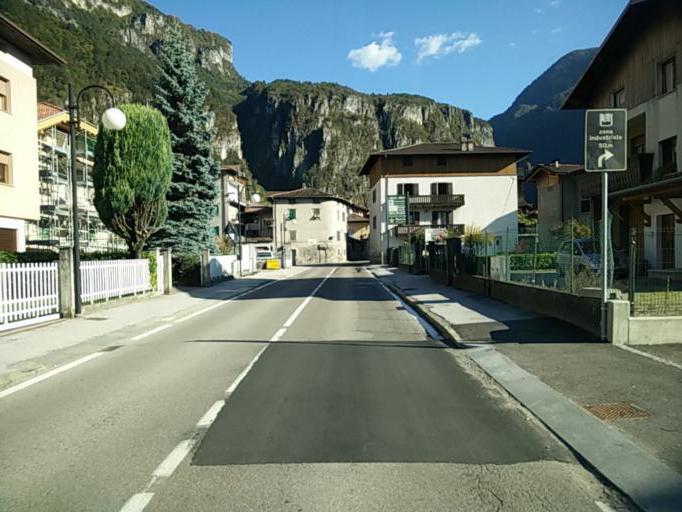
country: IT
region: Trentino-Alto Adige
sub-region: Provincia di Trento
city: Storo
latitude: 45.8493
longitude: 10.5767
